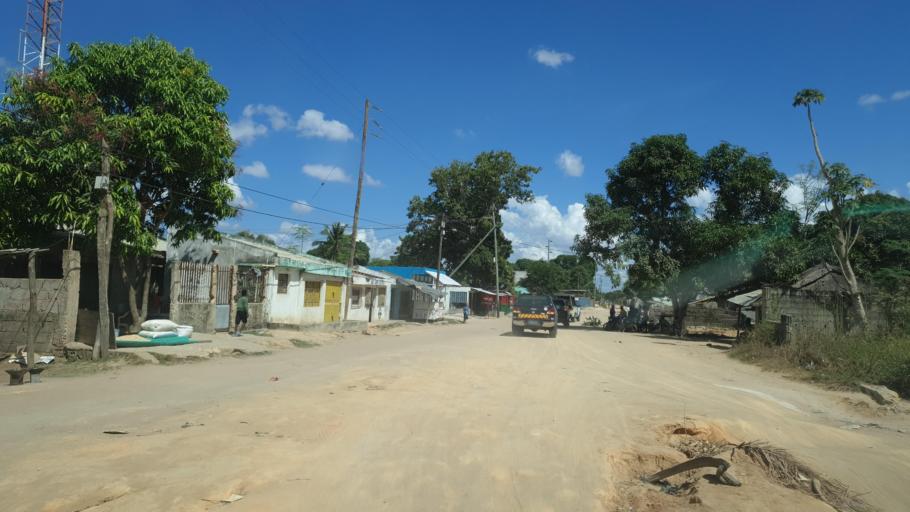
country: MZ
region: Nampula
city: Nacala
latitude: -14.5720
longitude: 40.6928
